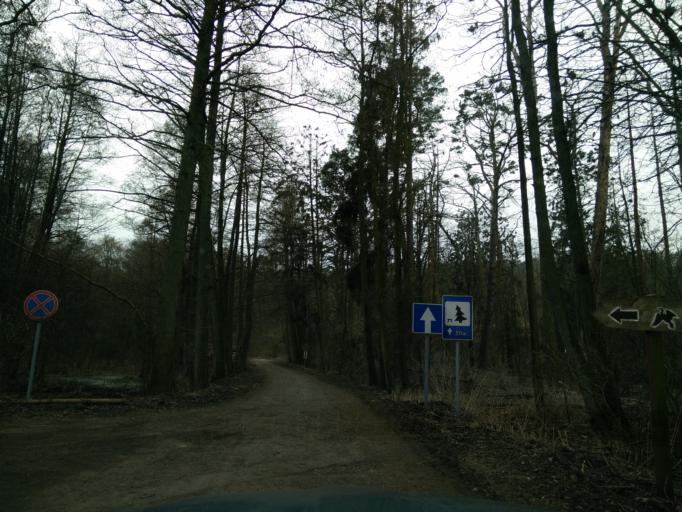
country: LT
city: Neringa
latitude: 55.5201
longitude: 21.1125
